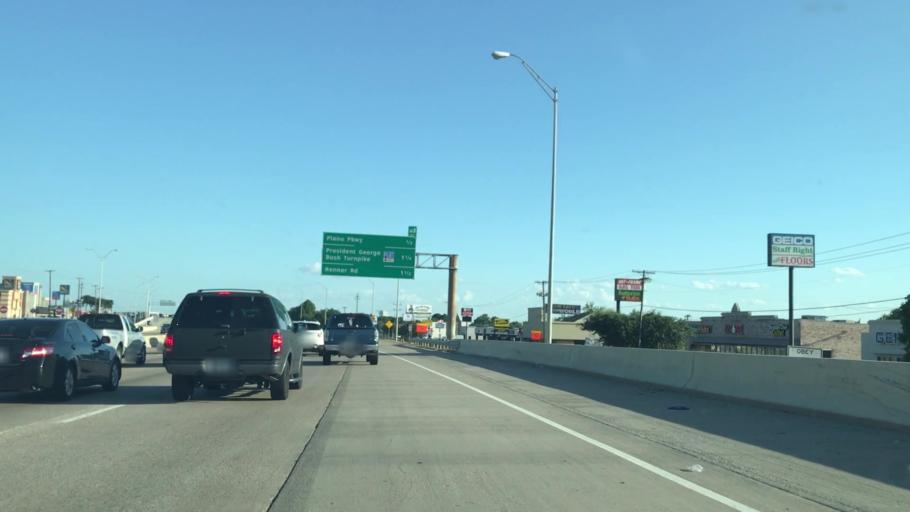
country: US
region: Texas
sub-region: Collin County
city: Plano
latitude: 33.0248
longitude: -96.7102
